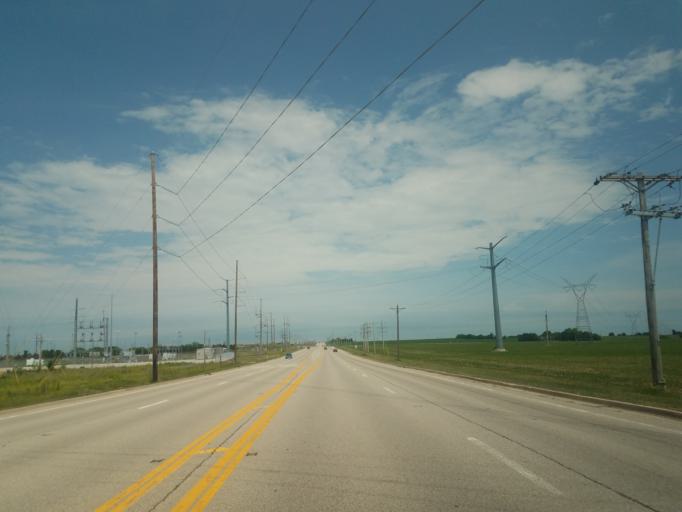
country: US
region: Illinois
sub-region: McLean County
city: Downs
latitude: 40.4515
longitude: -88.9017
